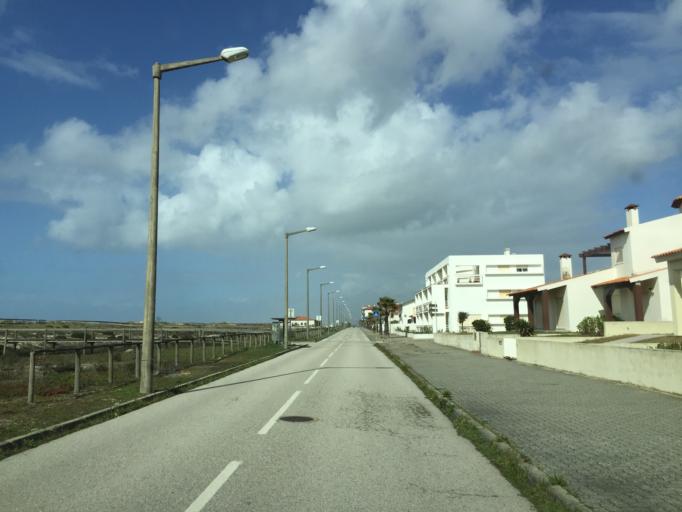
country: PT
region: Coimbra
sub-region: Figueira da Foz
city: Buarcos
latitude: 40.2127
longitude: -8.8945
